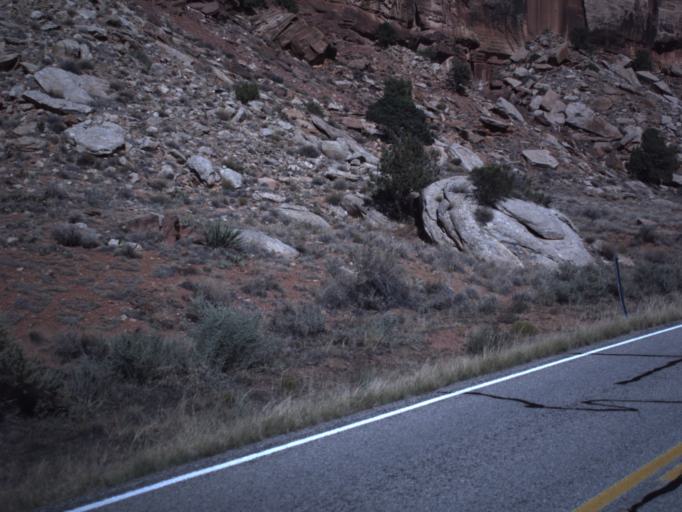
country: US
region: Utah
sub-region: San Juan County
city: Monticello
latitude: 38.0336
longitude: -109.5441
